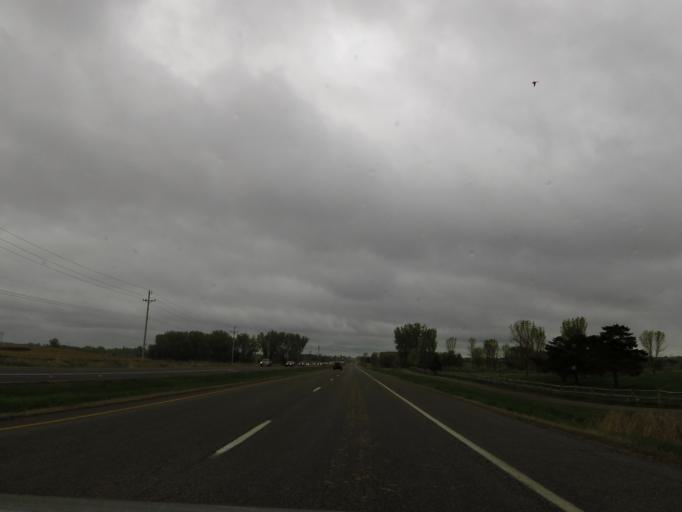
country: US
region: Minnesota
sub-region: Washington County
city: Oakdale
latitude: 44.9609
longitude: -92.9342
